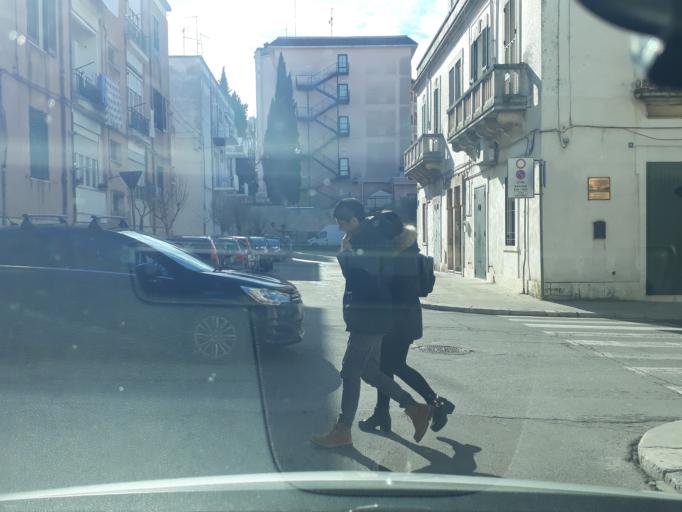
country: IT
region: Apulia
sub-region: Provincia di Taranto
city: Martina Franca
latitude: 40.7021
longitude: 17.3425
